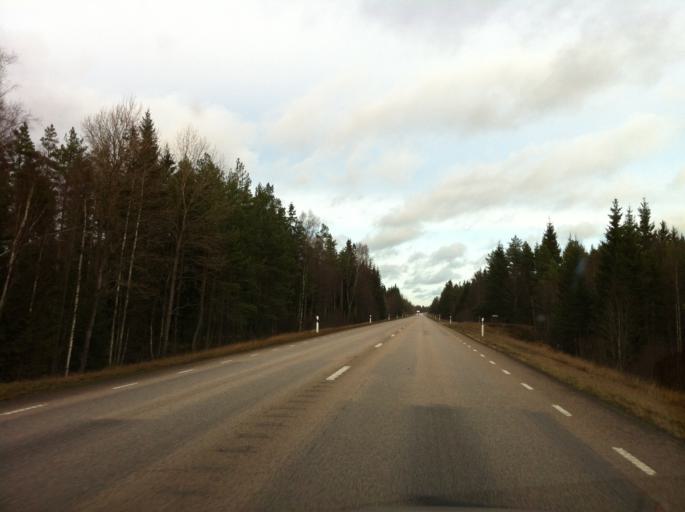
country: SE
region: Kronoberg
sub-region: Uppvidinge Kommun
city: Lenhovda
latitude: 57.1169
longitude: 15.2219
